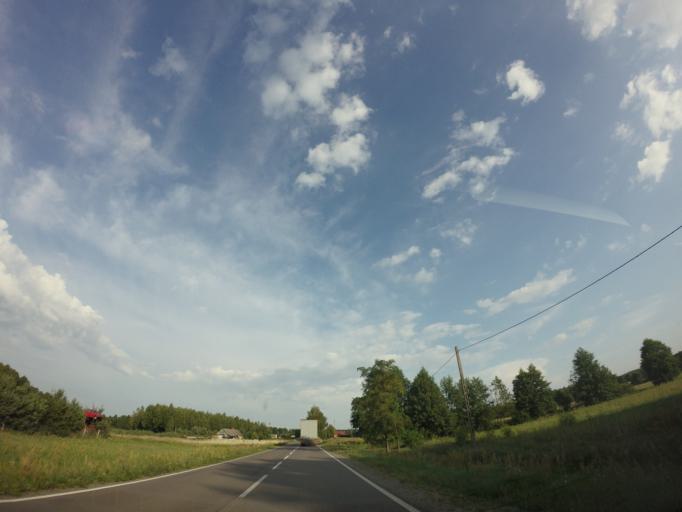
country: PL
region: Lublin Voivodeship
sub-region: Powiat lubartowski
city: Jeziorzany
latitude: 51.5761
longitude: 22.2868
